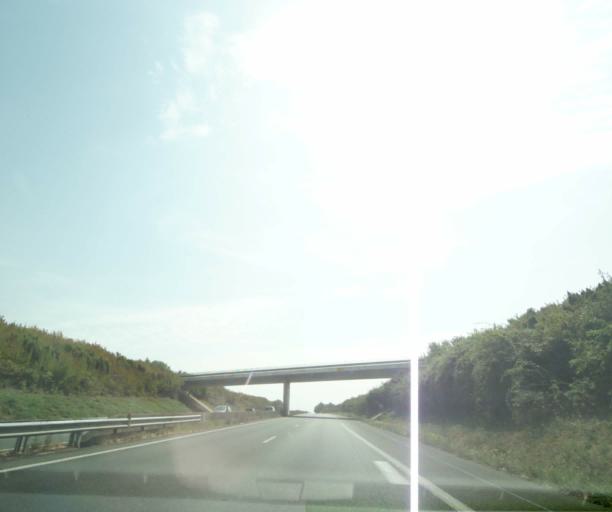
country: FR
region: Pays de la Loire
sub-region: Departement de la Vendee
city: Sainte-Hermine
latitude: 46.5659
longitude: -1.1087
